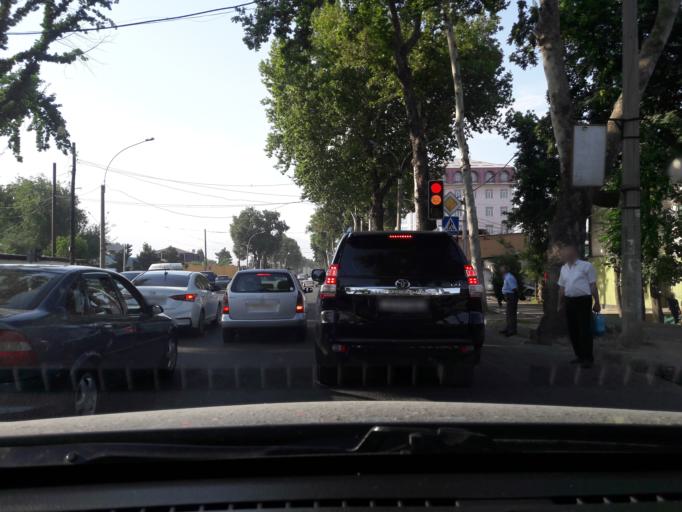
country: TJ
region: Dushanbe
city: Dushanbe
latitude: 38.5399
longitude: 68.7718
